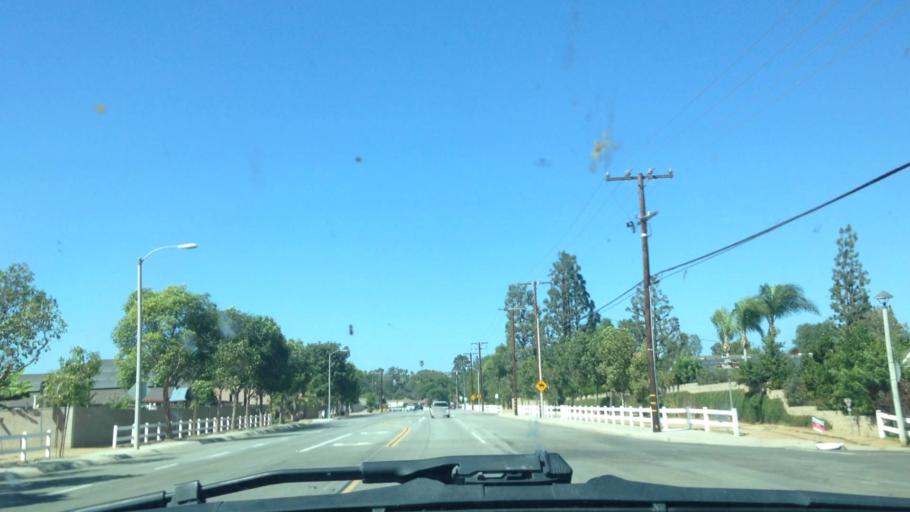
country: US
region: California
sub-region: Orange County
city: Yorba Linda
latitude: 33.8777
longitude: -117.8161
